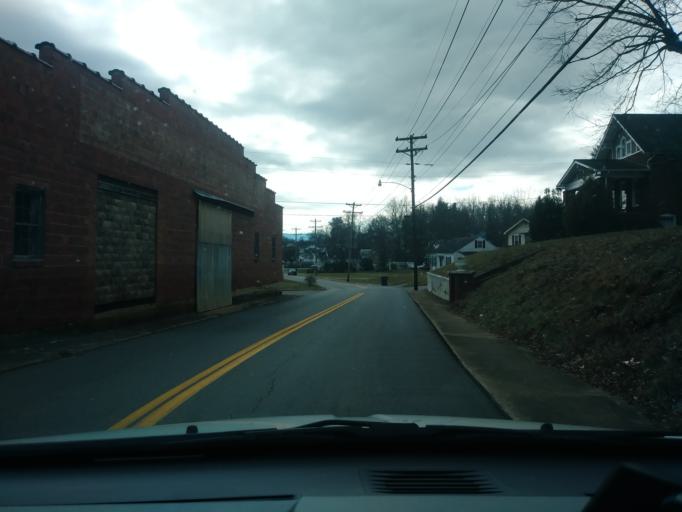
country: US
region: Tennessee
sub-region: Greene County
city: Greeneville
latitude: 36.1595
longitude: -82.8293
